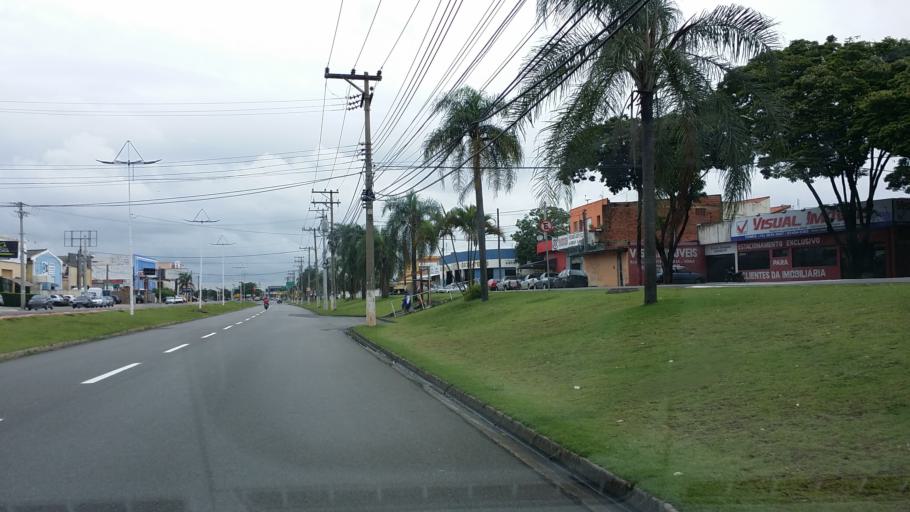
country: BR
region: Sao Paulo
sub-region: Indaiatuba
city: Indaiatuba
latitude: -23.1164
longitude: -47.2227
